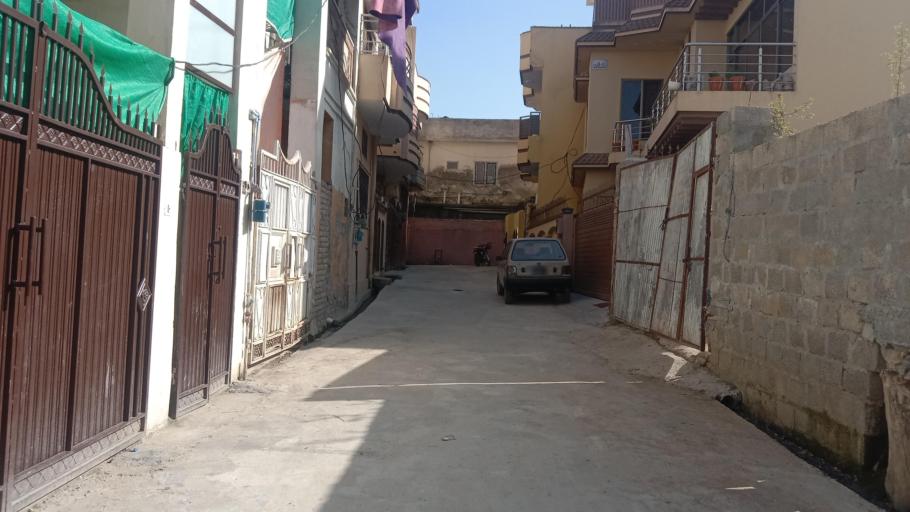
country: PK
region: Khyber Pakhtunkhwa
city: Abbottabad
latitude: 34.1781
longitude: 73.2245
